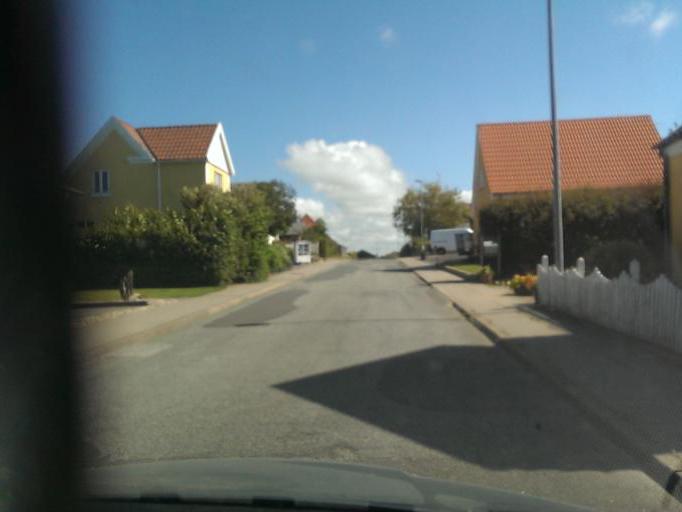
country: DK
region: North Denmark
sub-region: Jammerbugt Kommune
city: Pandrup
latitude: 57.3134
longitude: 9.7116
